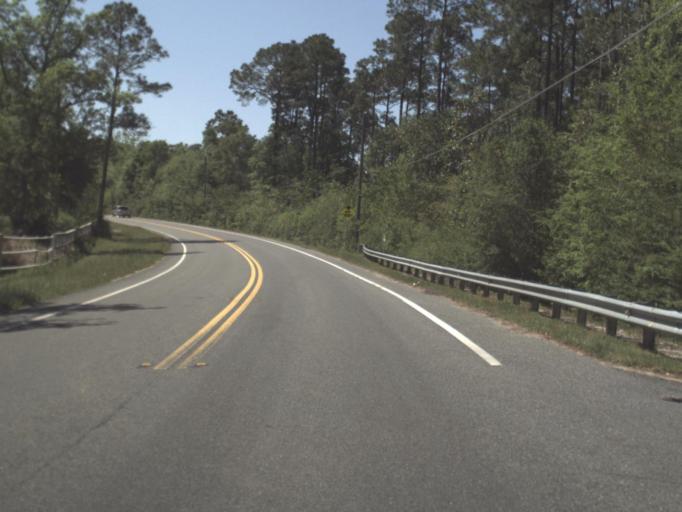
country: US
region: Florida
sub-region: Escambia County
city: Cantonment
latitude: 30.5338
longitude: -87.3977
